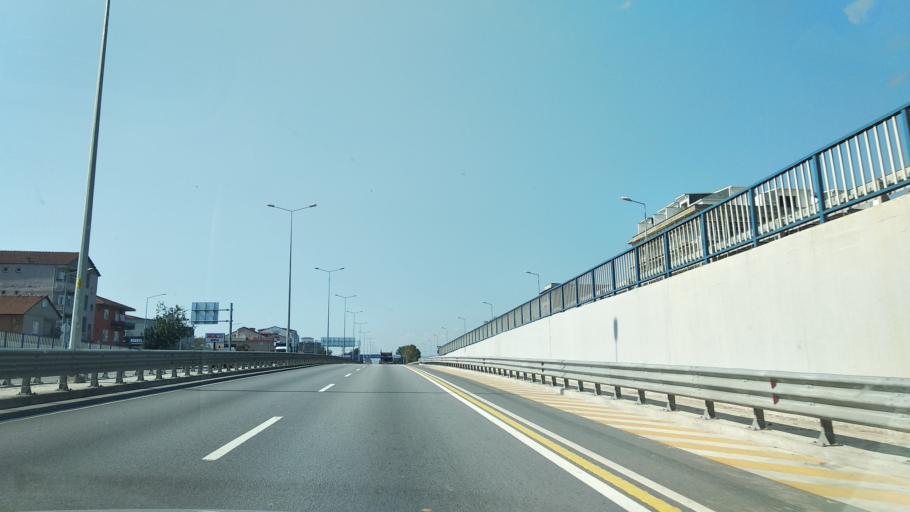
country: TR
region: Kocaeli
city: Kosekoy
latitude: 40.7538
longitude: 30.0214
